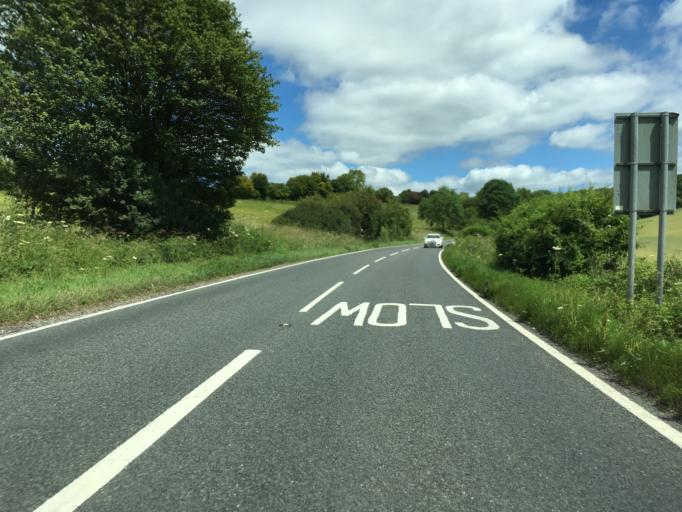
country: GB
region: England
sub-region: Hampshire
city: Highclere
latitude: 51.3081
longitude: -1.3965
